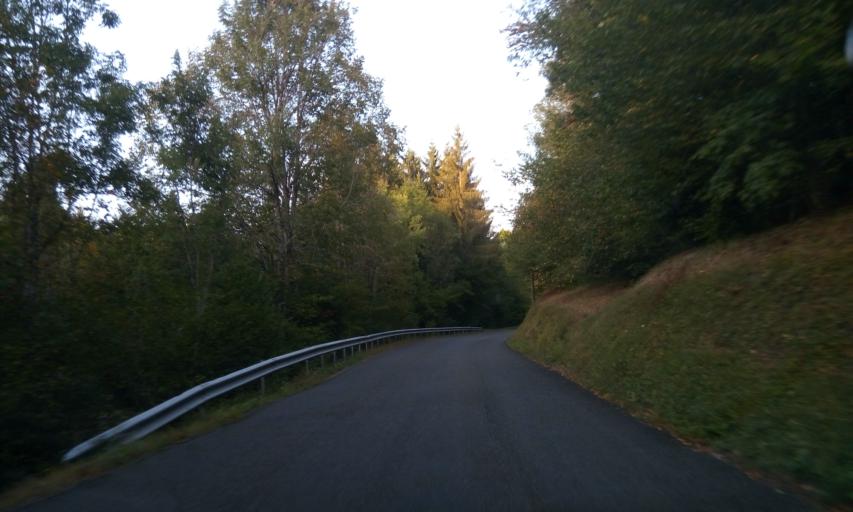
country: FR
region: Rhone-Alpes
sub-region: Departement de l'Ain
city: Nantua
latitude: 46.1764
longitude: 5.6796
